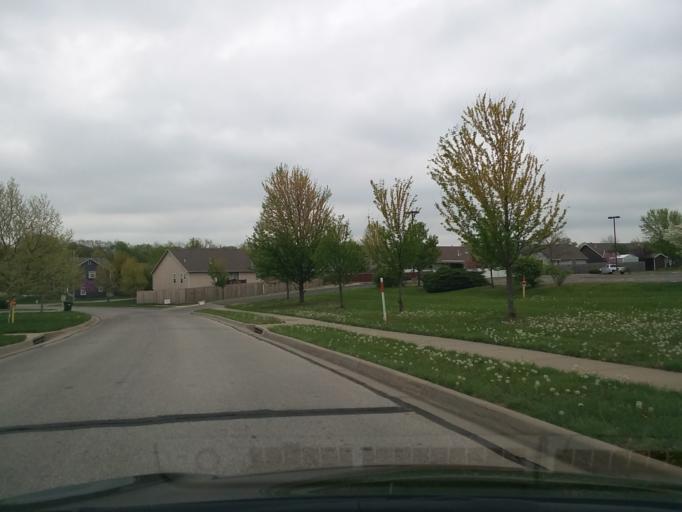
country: US
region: Kansas
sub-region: Douglas County
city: Lawrence
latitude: 38.9916
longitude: -95.2784
